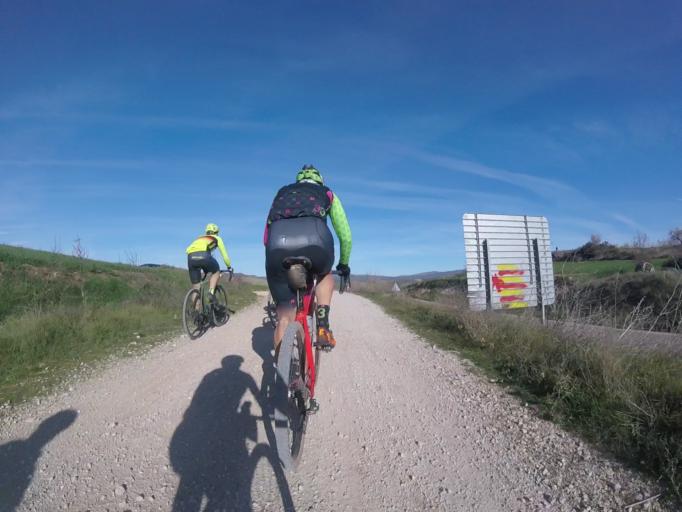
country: ES
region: Navarre
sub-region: Provincia de Navarra
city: Yerri
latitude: 42.6825
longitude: -1.9596
